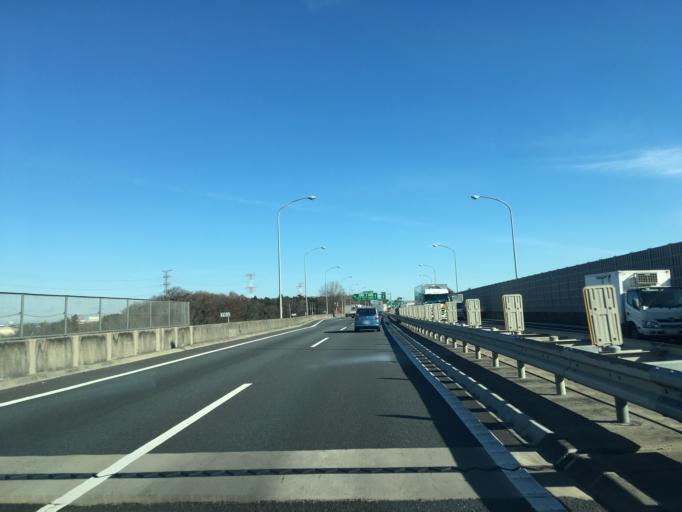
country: JP
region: Saitama
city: Sakado
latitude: 35.9270
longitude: 139.3948
